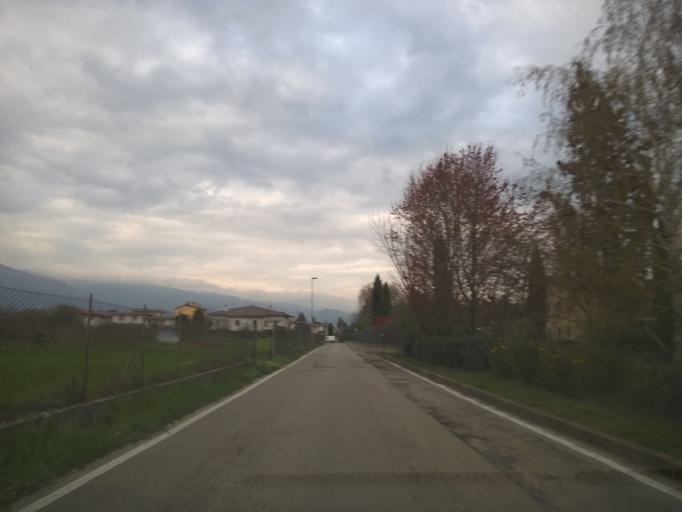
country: IT
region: Veneto
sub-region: Provincia di Vicenza
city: Thiene
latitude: 45.6959
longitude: 11.4736
